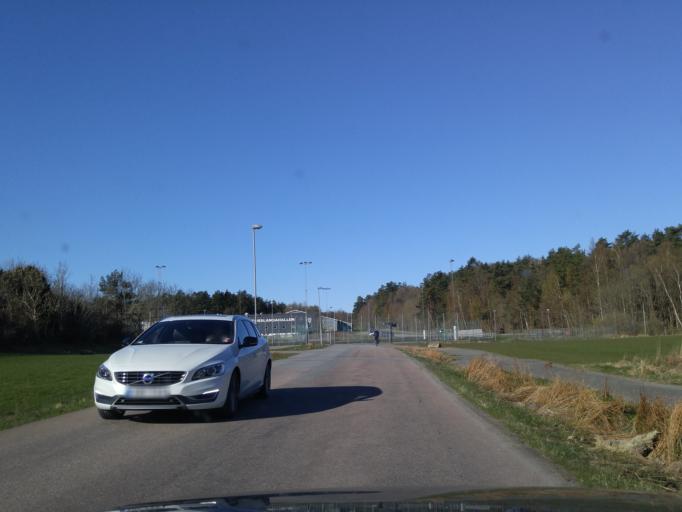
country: SE
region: Vaestra Goetaland
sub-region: Goteborg
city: Torslanda
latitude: 57.7198
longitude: 11.7606
